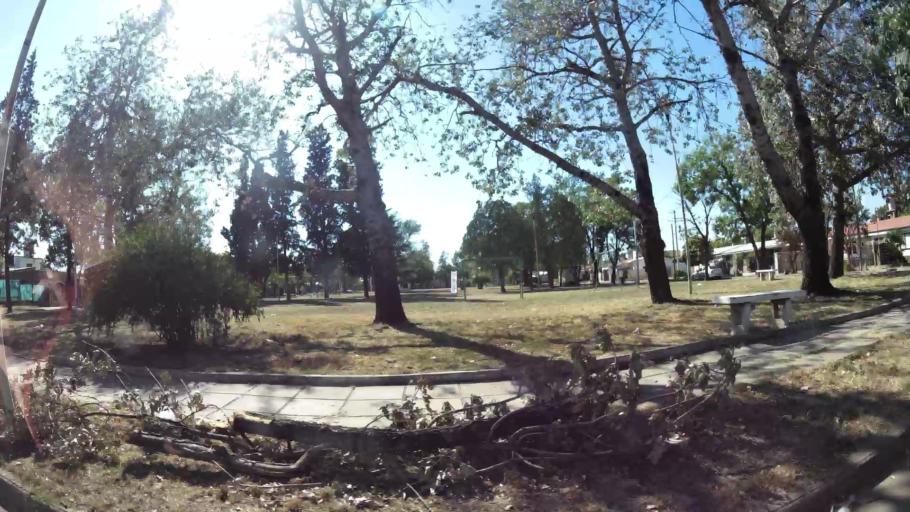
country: AR
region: Cordoba
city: Villa Allende
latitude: -31.3416
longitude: -64.2400
